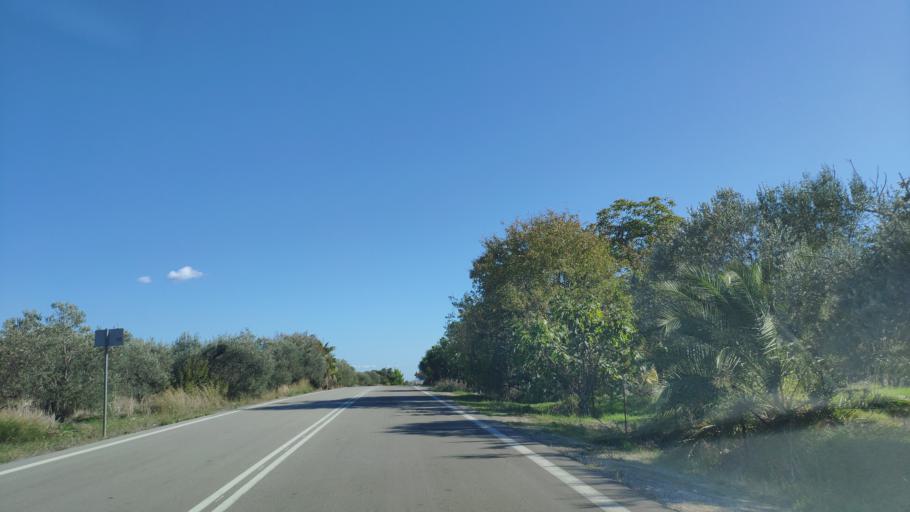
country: GR
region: Peloponnese
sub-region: Nomos Argolidos
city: Palaia Epidavros
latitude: 37.5760
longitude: 23.2452
